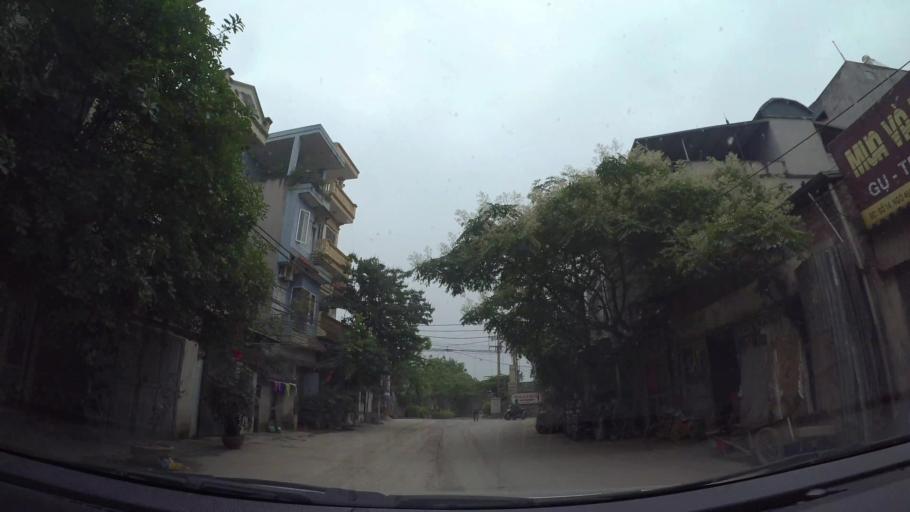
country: VN
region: Ha Noi
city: Tay Ho
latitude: 21.0817
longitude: 105.8202
